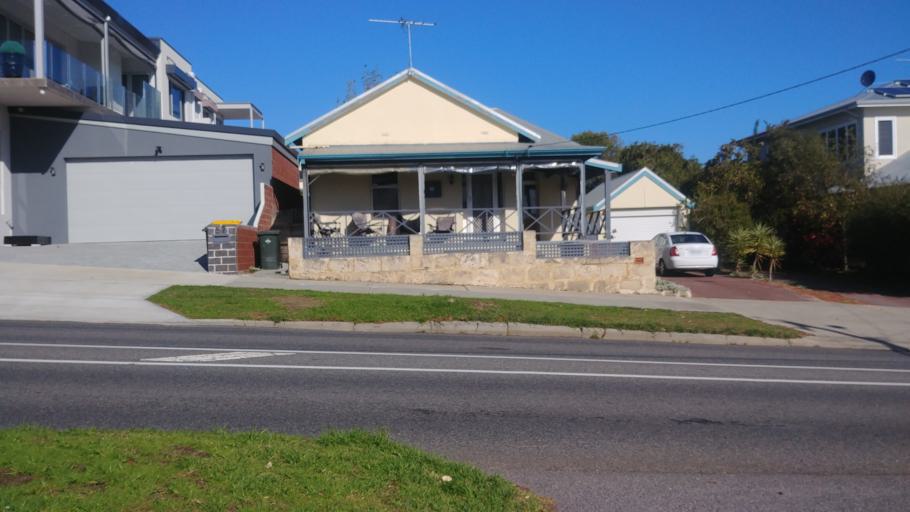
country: AU
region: Western Australia
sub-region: Fremantle
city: South Fremantle
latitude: -32.0675
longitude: 115.7609
